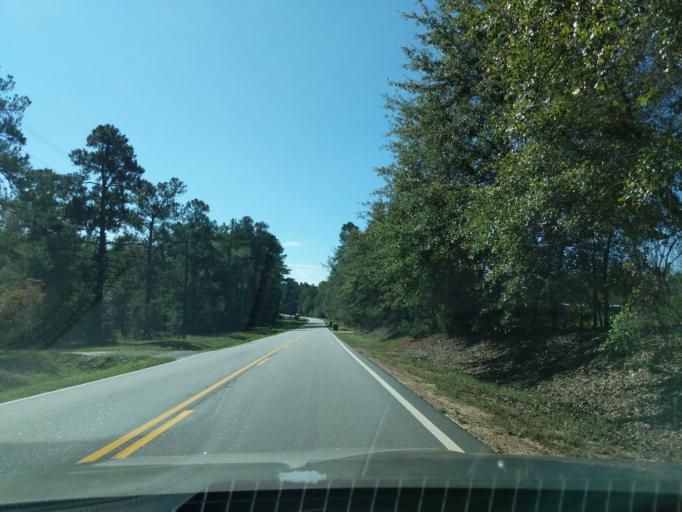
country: US
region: Georgia
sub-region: Richmond County
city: Hephzibah
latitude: 33.2946
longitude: -82.0221
